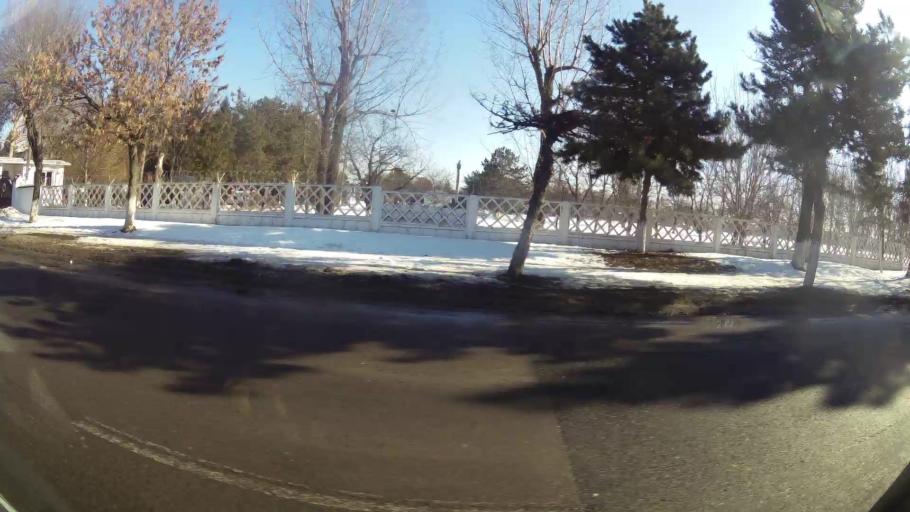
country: RO
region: Ilfov
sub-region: Comuna Magurele
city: Magurele
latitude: 44.3902
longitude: 26.0476
